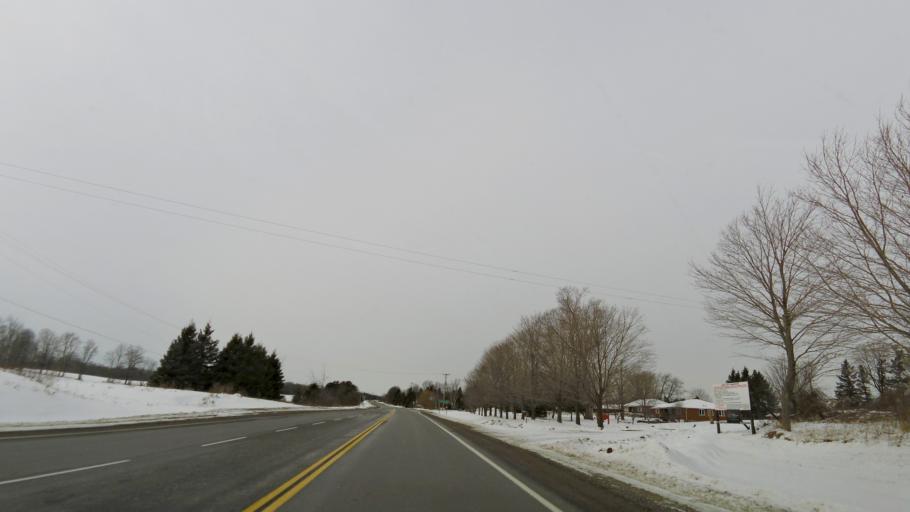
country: CA
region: Ontario
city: Ancaster
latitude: 43.2972
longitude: -80.1159
